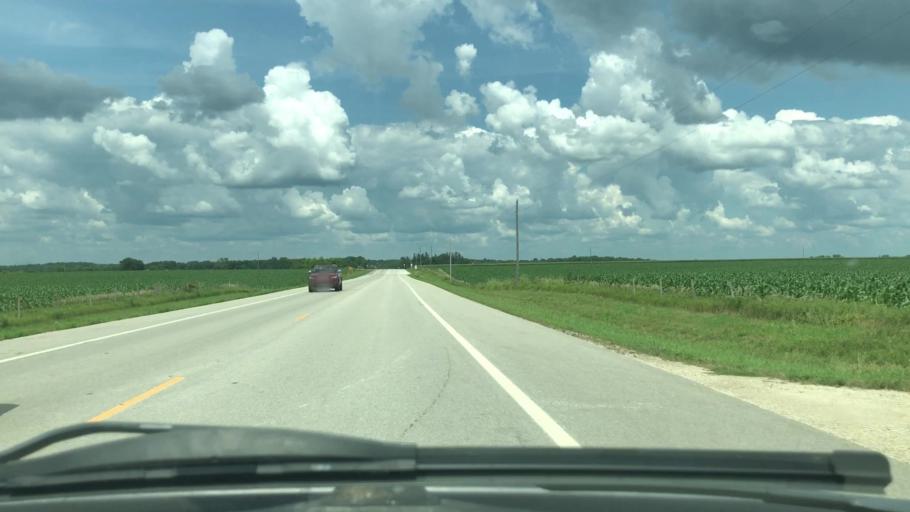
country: US
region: Minnesota
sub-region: Olmsted County
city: Rochester
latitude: 43.9605
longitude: -92.5183
